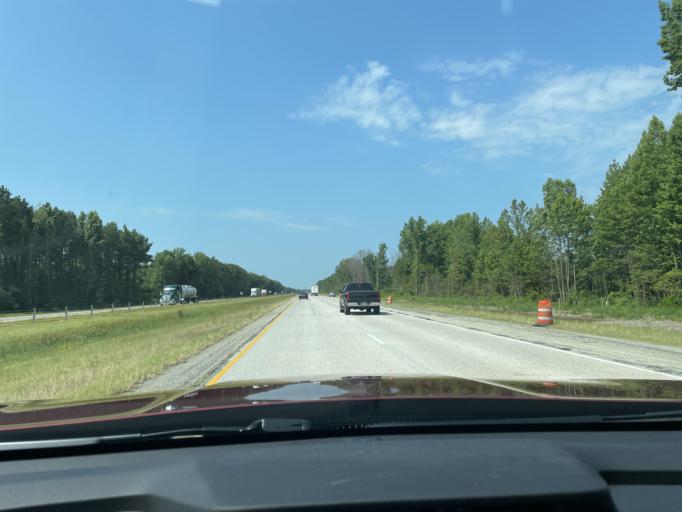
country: US
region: Arkansas
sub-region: White County
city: Searcy
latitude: 35.1648
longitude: -91.7767
